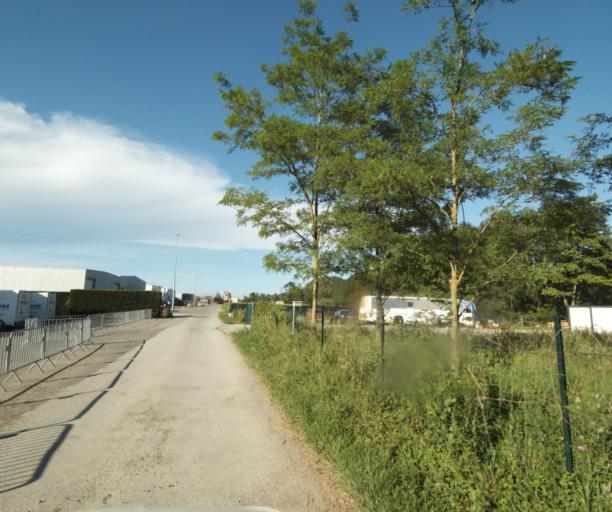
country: FR
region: Rhone-Alpes
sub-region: Departement de la Haute-Savoie
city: Loisin
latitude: 46.2934
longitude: 6.3014
